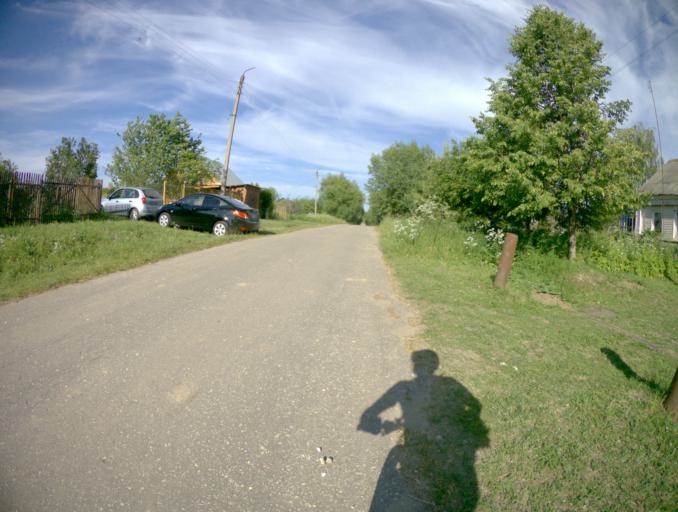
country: RU
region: Vladimir
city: Vorsha
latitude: 56.1720
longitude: 40.1682
